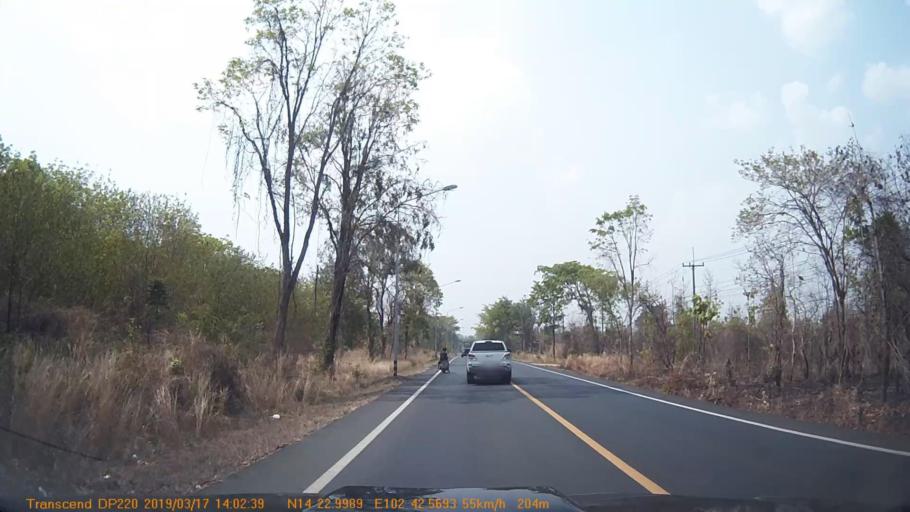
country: TH
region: Buriram
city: Pa Kham
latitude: 14.3835
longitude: 102.7093
